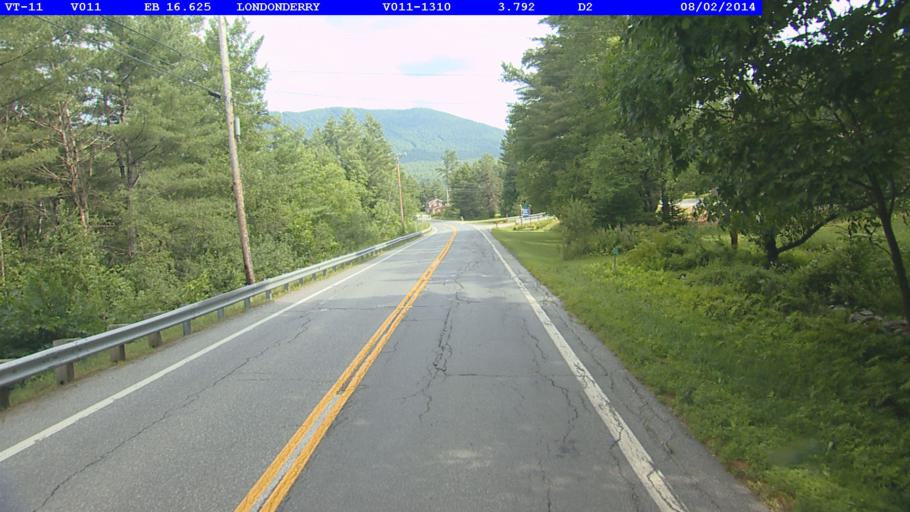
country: US
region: Vermont
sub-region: Windsor County
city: Chester
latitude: 43.2138
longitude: -72.7882
